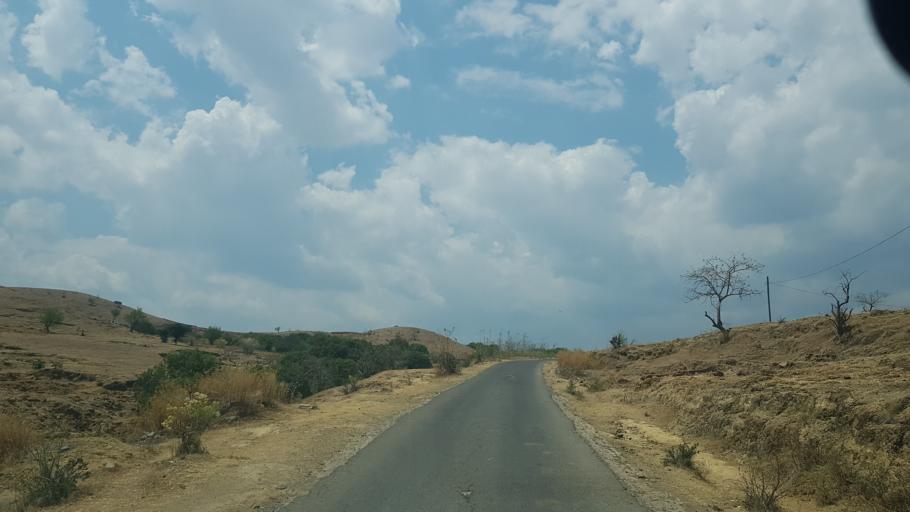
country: MX
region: Puebla
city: San Juan Amecac
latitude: 18.8105
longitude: -98.6240
